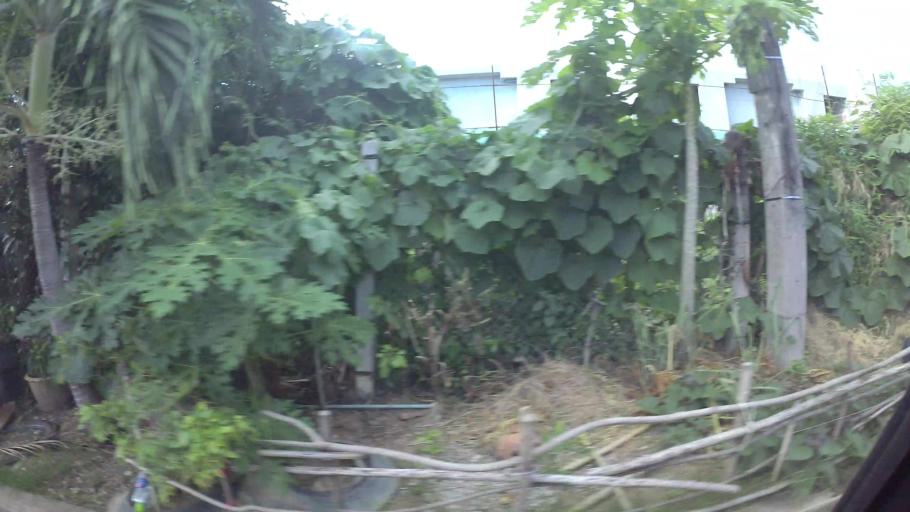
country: TH
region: Chon Buri
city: Phatthaya
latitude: 12.9092
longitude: 100.8761
